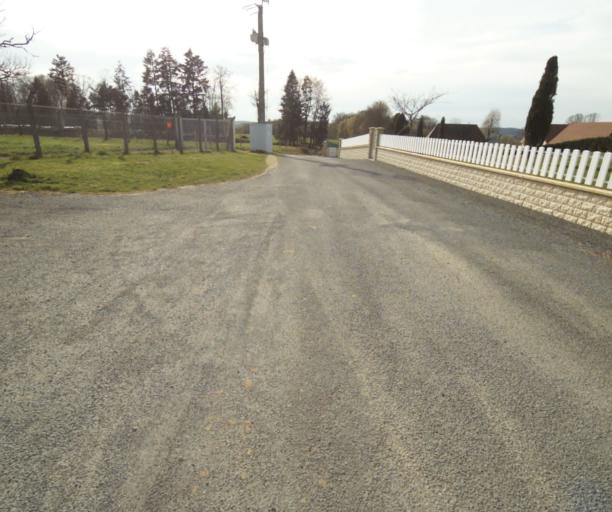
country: FR
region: Limousin
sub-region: Departement de la Correze
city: Naves
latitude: 45.2926
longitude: 1.7423
